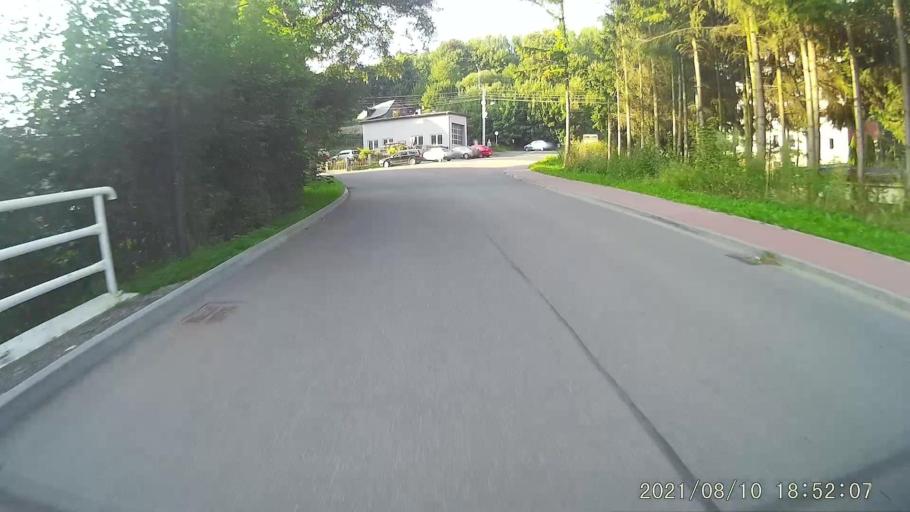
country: PL
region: Lower Silesian Voivodeship
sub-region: Powiat klodzki
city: Duszniki-Zdroj
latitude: 50.4089
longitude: 16.3831
